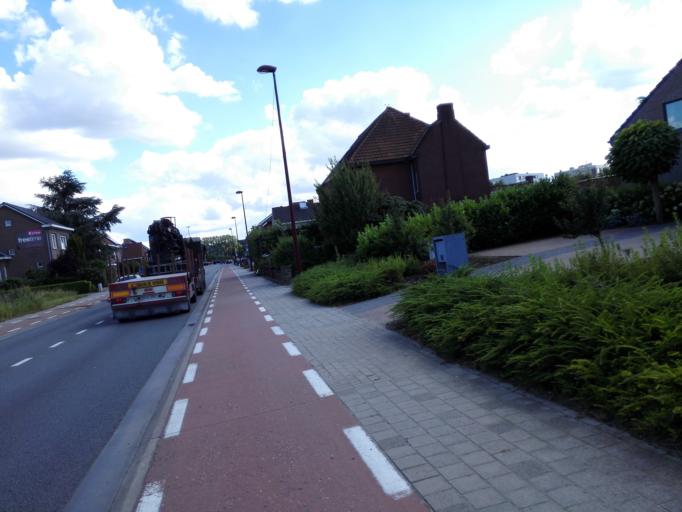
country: BE
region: Flanders
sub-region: Provincie Vlaams-Brabant
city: Aarschot
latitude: 50.9949
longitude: 4.8427
